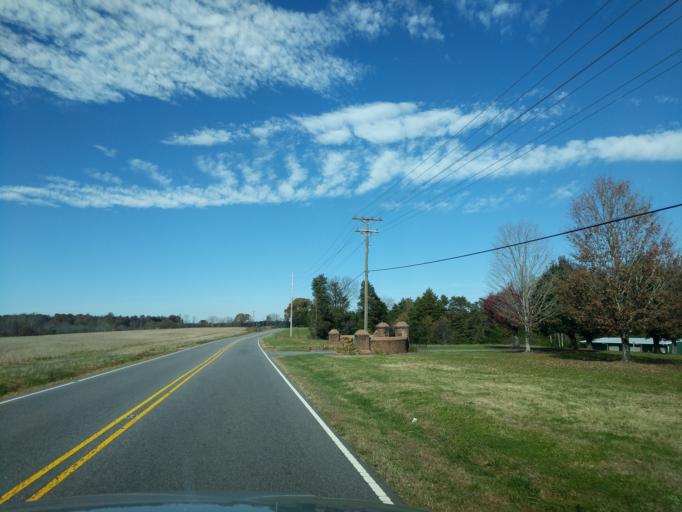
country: US
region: North Carolina
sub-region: Catawba County
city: Maiden
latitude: 35.6109
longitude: -81.2560
